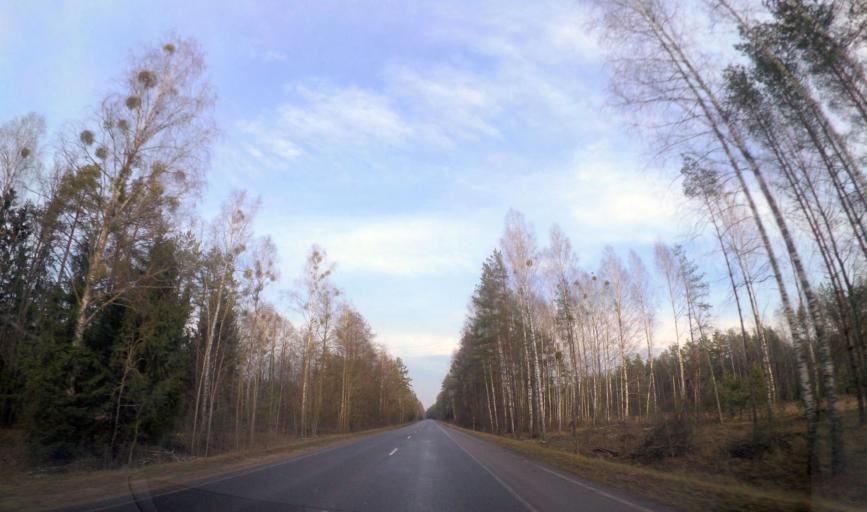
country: LT
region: Alytaus apskritis
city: Druskininkai
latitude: 53.8676
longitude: 24.1149
